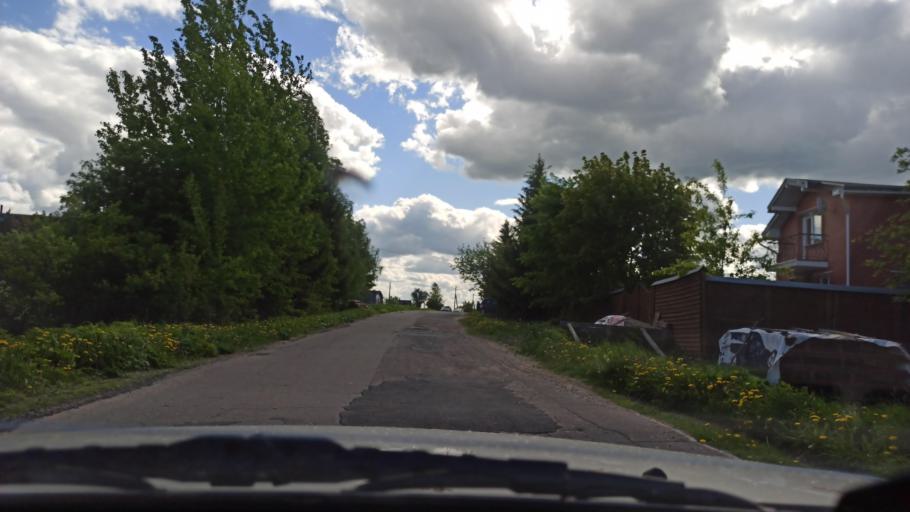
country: RU
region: Vologda
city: Molochnoye
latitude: 59.3787
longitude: 39.7178
